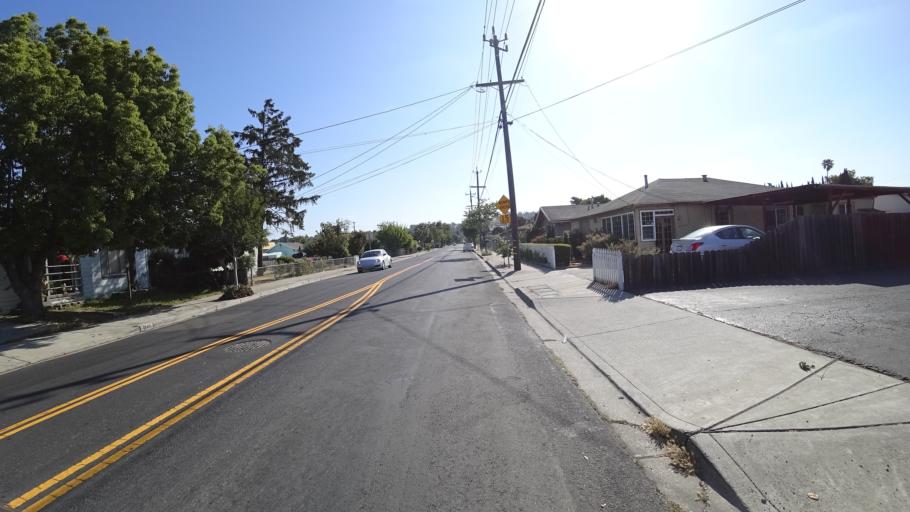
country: US
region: California
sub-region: Alameda County
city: Hayward
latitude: 37.6563
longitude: -122.0817
